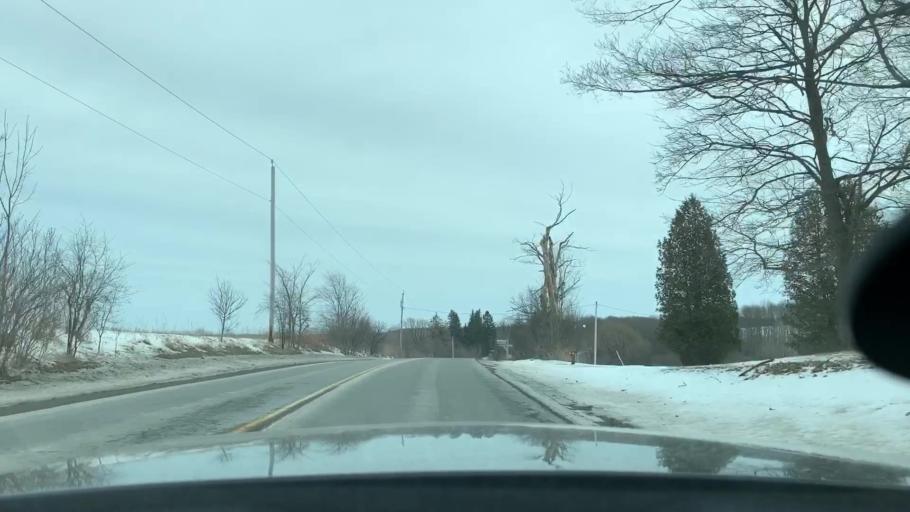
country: US
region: New York
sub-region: Oneida County
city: Washington Mills
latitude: 43.0477
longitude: -75.2264
